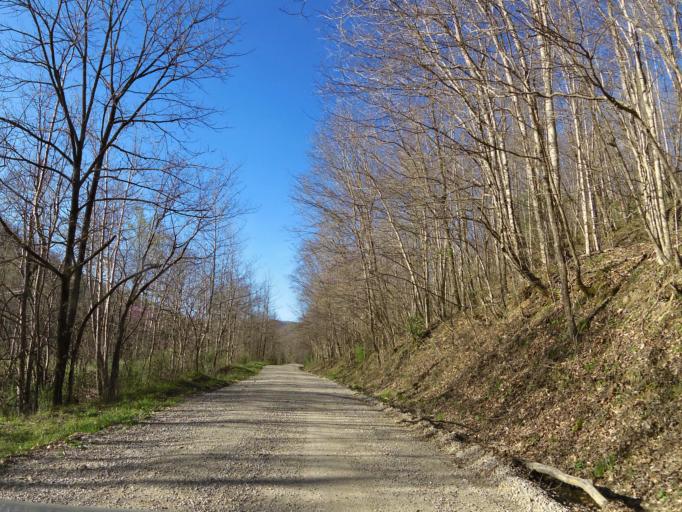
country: US
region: Tennessee
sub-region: Roane County
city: Oliver Springs
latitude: 36.2179
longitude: -84.4158
